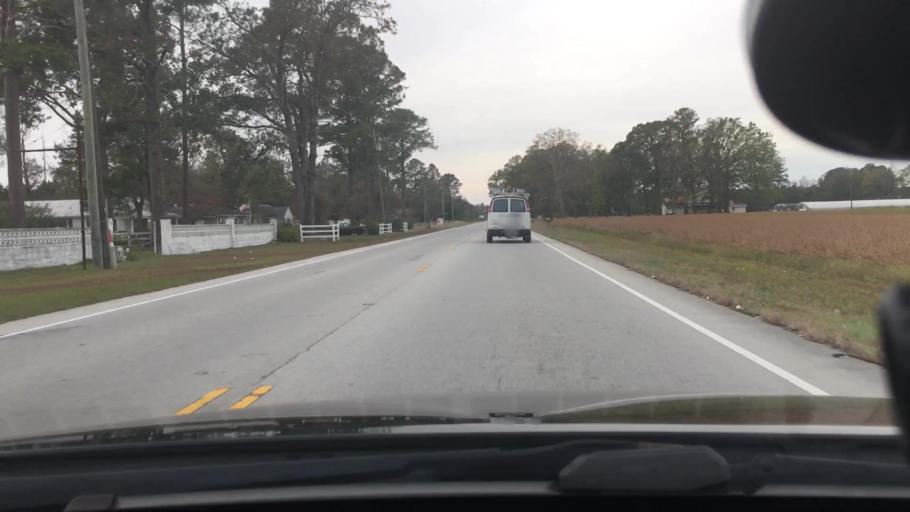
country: US
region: North Carolina
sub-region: Craven County
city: Vanceboro
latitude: 35.2403
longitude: -77.0786
